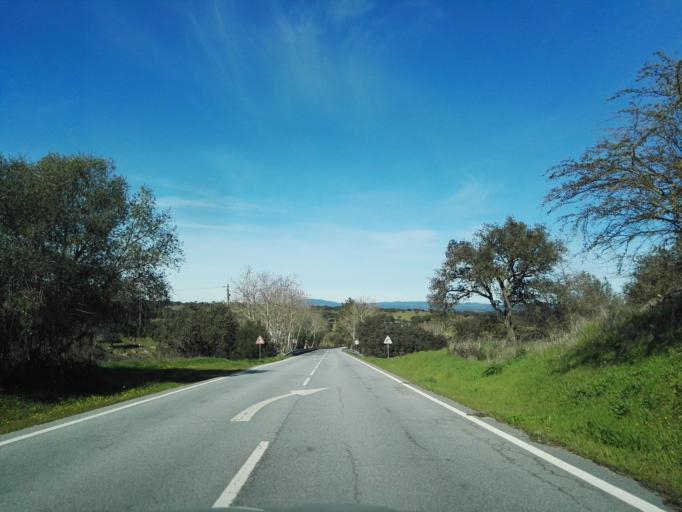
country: PT
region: Portalegre
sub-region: Arronches
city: Arronches
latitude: 39.0881
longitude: -7.2831
